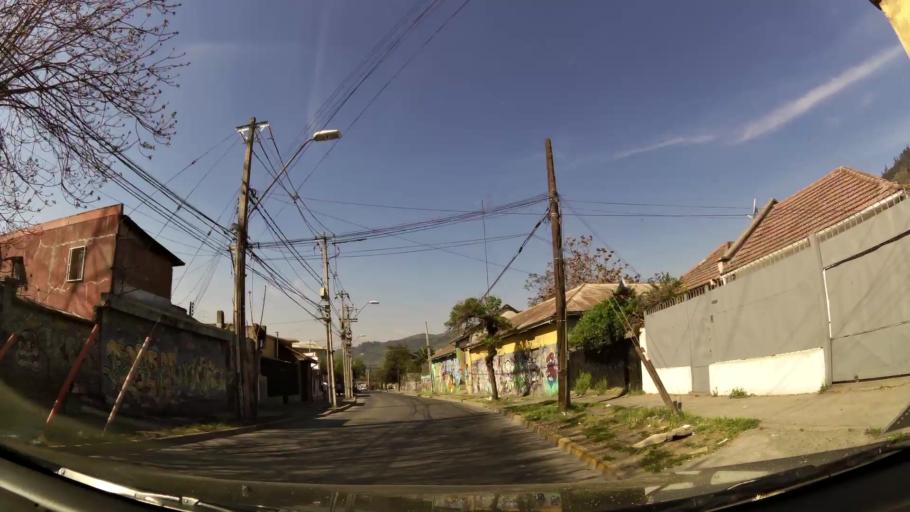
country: CL
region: Santiago Metropolitan
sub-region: Provincia de Santiago
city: Santiago
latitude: -33.4126
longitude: -70.6352
